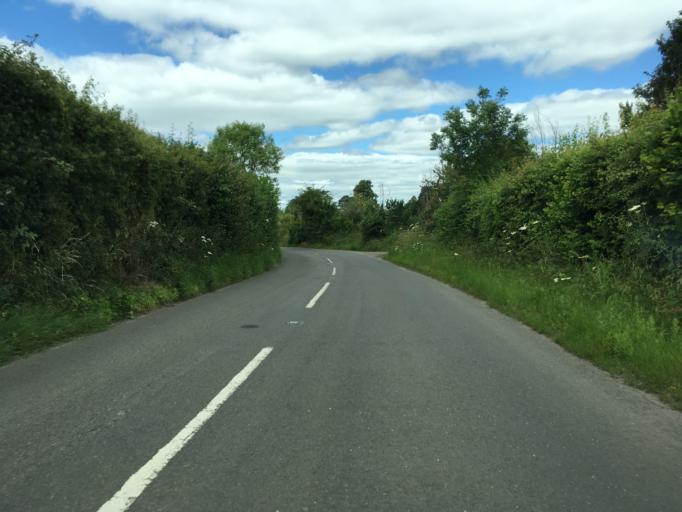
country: GB
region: England
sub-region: West Berkshire
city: Winterbourne
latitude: 51.4187
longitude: -1.3588
